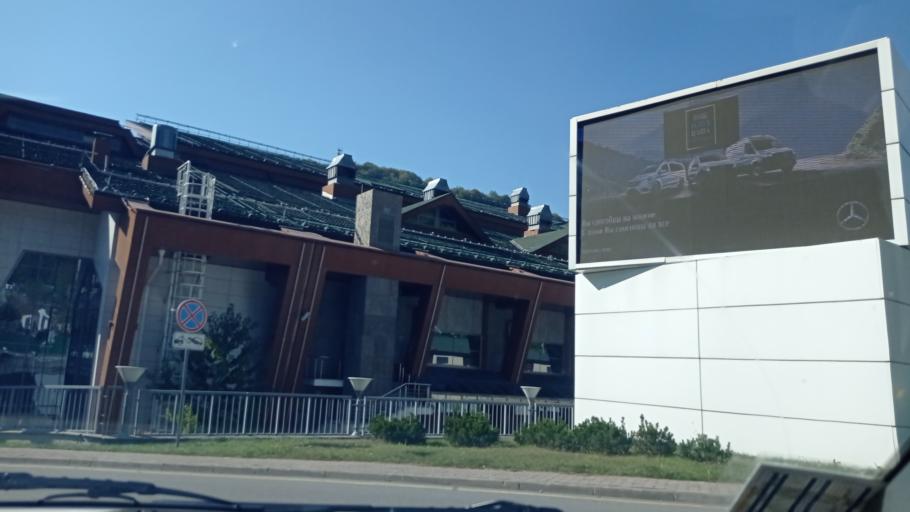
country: RU
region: Krasnodarskiy
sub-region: Sochi City
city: Krasnaya Polyana
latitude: 43.6860
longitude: 40.2804
